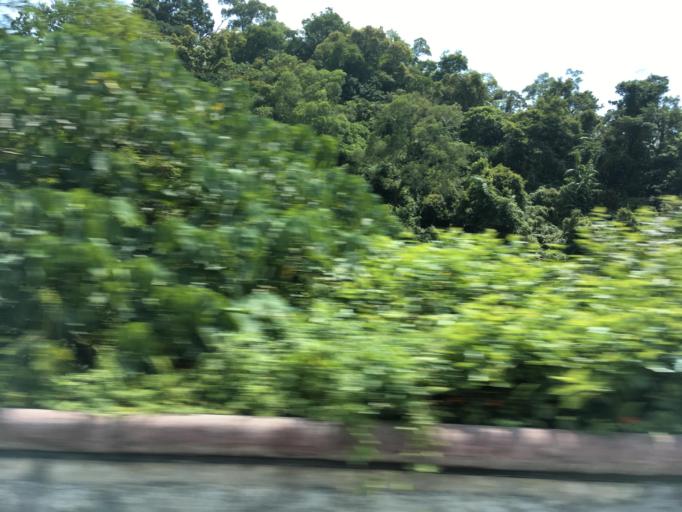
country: TW
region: Taiwan
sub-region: Yilan
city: Yilan
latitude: 24.8178
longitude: 121.7470
